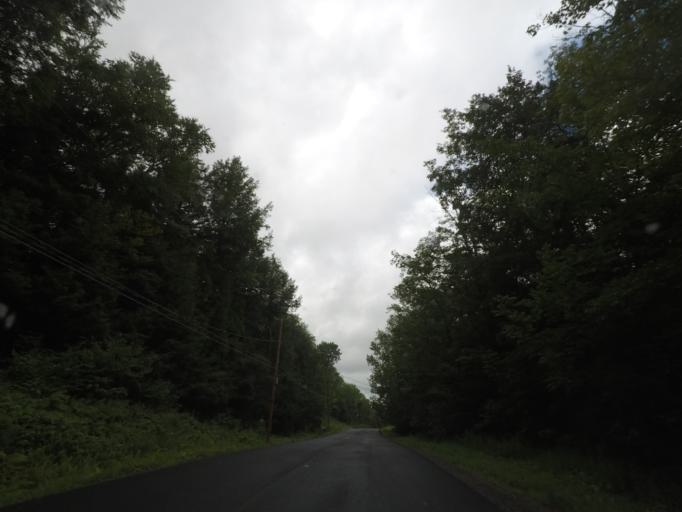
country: US
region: New York
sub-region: Rensselaer County
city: Poestenkill
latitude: 42.6909
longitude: -73.4611
